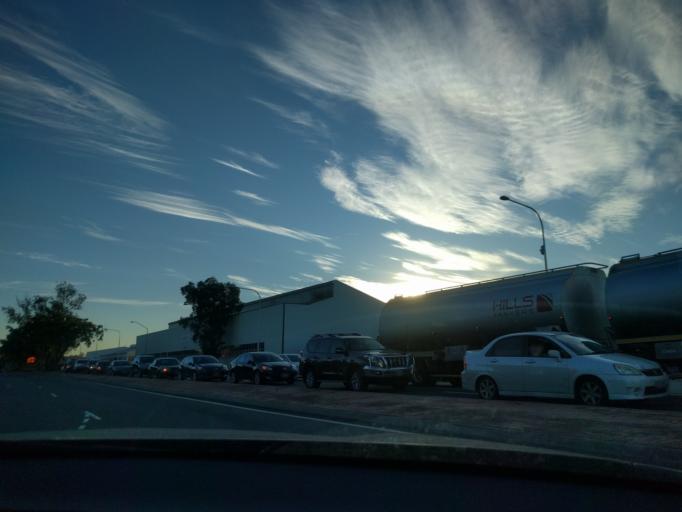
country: AU
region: Queensland
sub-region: Brisbane
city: Ascot
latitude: -27.4318
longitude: 153.0878
